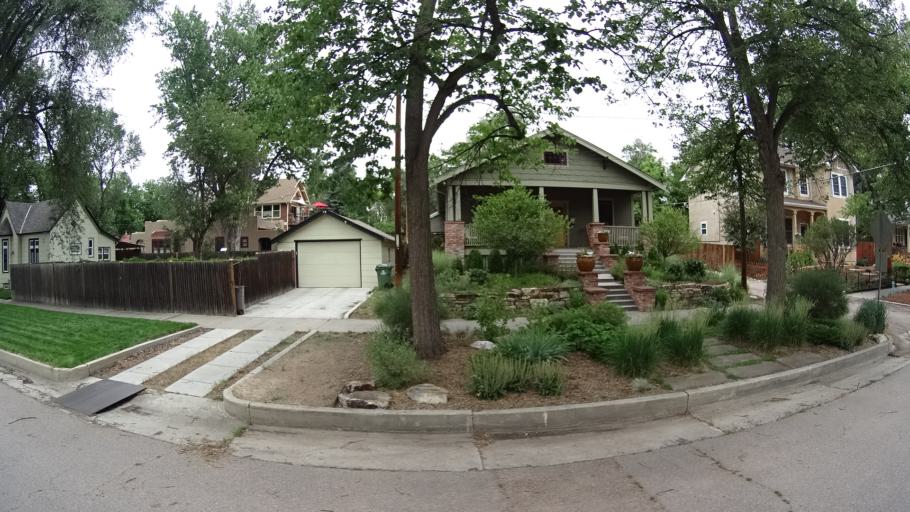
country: US
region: Colorado
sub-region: El Paso County
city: Colorado Springs
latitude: 38.8450
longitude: -104.8061
